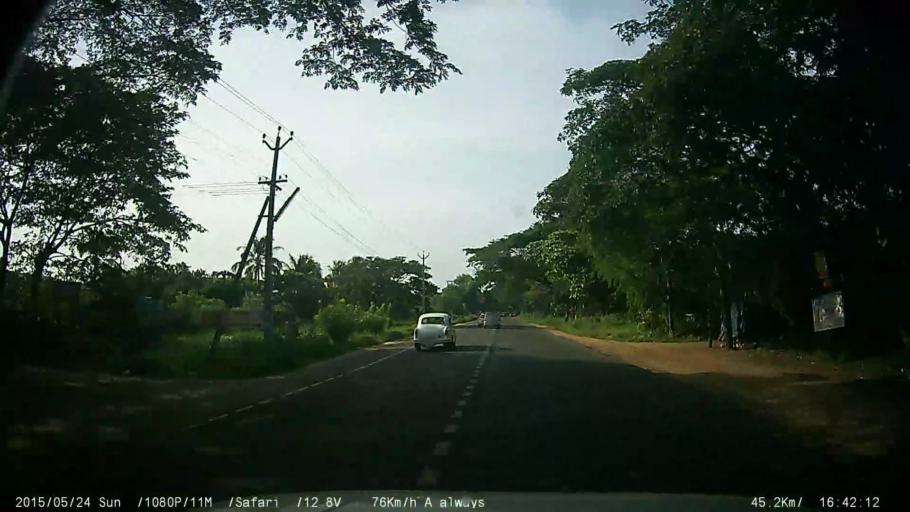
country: IN
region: Kerala
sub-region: Alappuzha
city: Shertallai
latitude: 9.6383
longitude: 76.3348
